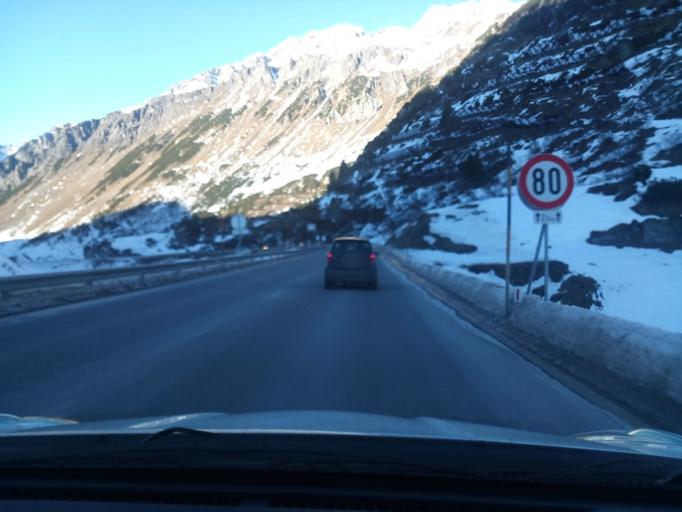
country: AT
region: Tyrol
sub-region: Politischer Bezirk Landeck
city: Sankt Anton am Arlberg
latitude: 47.1298
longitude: 10.2107
